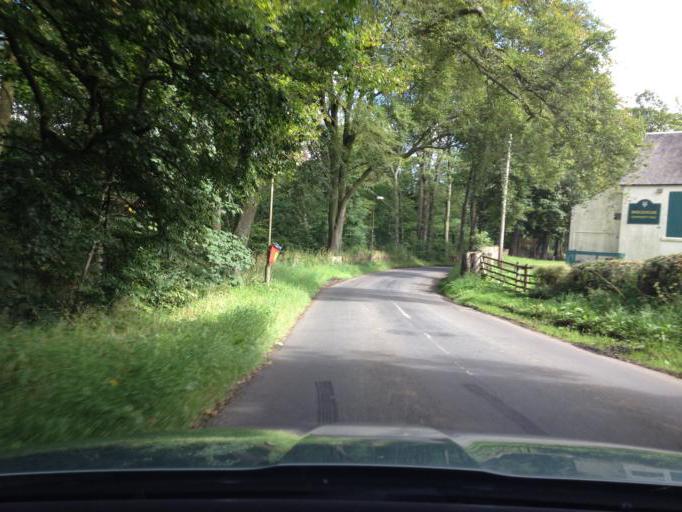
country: GB
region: Scotland
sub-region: West Lothian
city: Armadale
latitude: 55.9215
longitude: -3.6994
